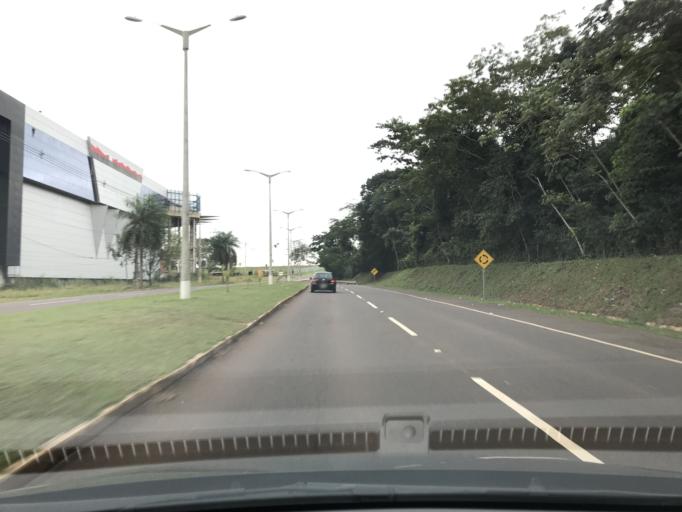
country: PY
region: Canindeyu
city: Salto del Guaira
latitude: -24.0085
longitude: -54.3237
